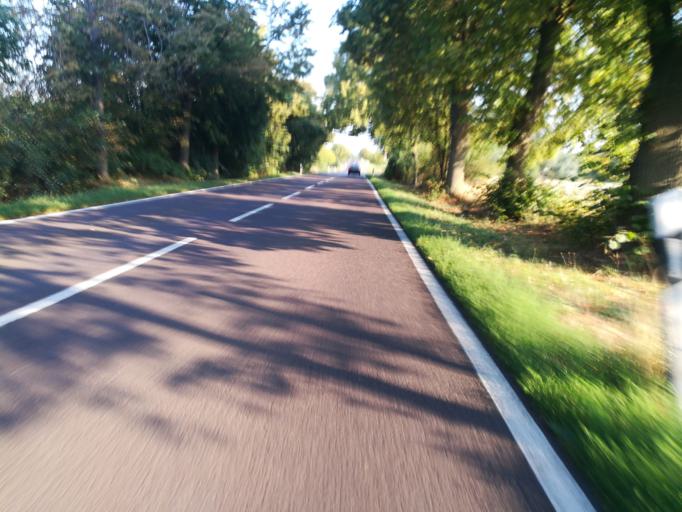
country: DE
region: Saxony-Anhalt
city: Haldensleben I
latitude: 52.2535
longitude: 11.4314
